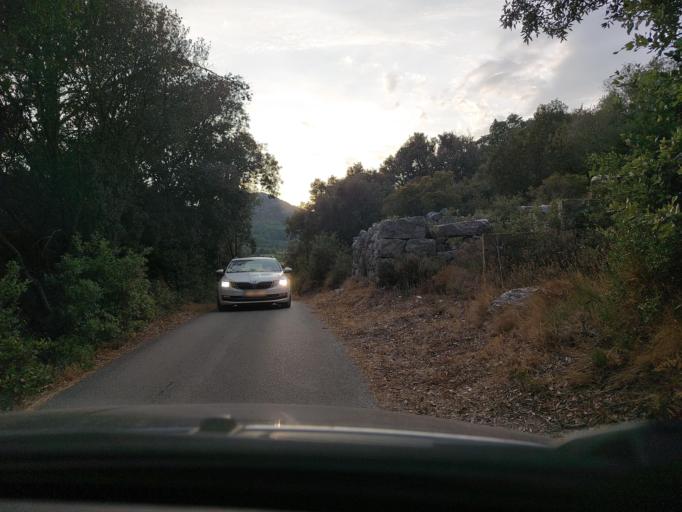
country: HR
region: Dubrovacko-Neretvanska
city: Smokvica
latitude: 42.7548
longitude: 16.9224
